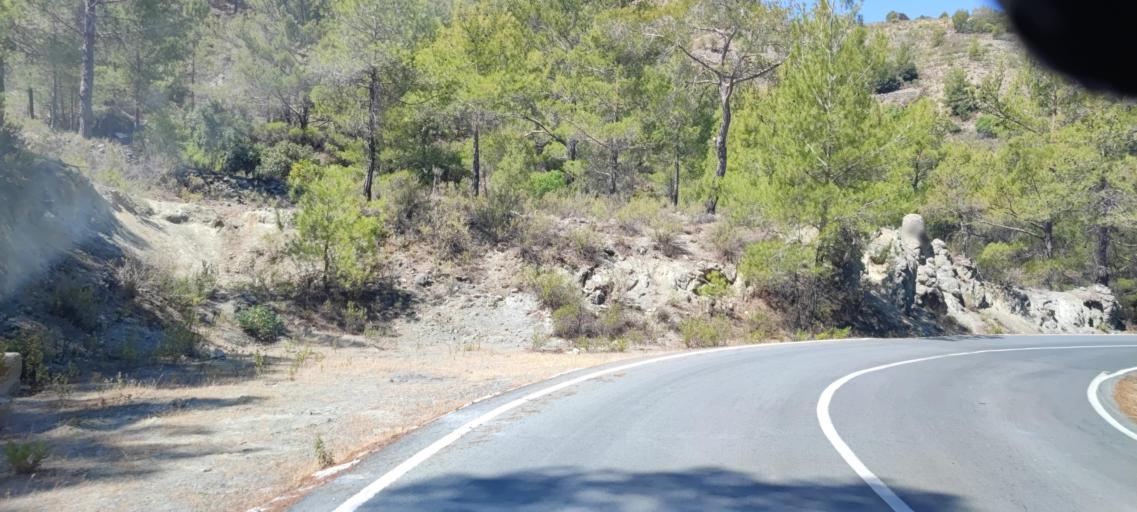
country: CY
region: Lefkosia
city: Kakopetria
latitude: 34.9189
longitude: 32.8126
